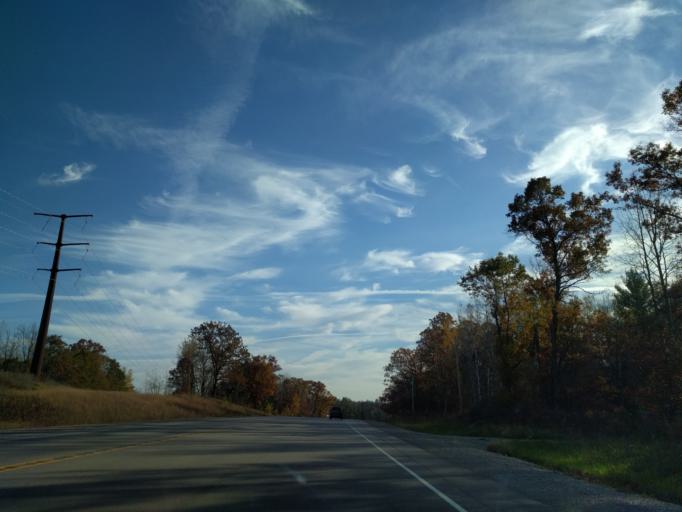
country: US
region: Wisconsin
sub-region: Marinette County
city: Peshtigo
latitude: 45.2619
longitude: -87.9905
